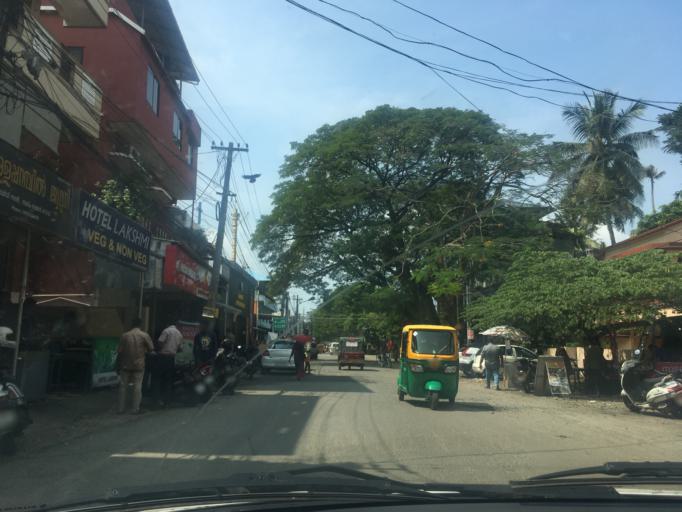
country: IN
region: Kerala
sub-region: Ernakulam
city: Cochin
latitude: 9.9777
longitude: 76.2951
